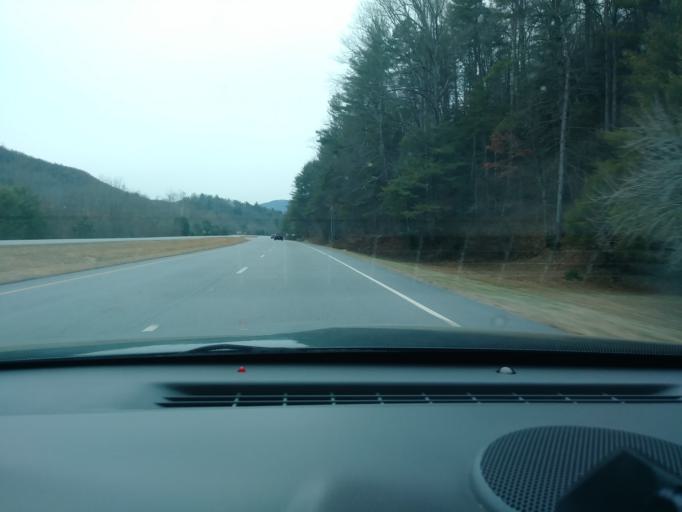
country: US
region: North Carolina
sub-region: Wilkes County
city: Millers Creek
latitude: 36.1845
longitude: -81.4018
